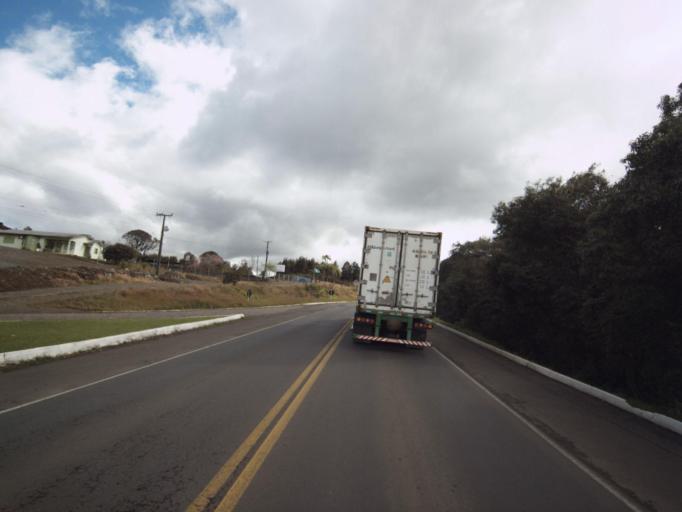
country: BR
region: Santa Catarina
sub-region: Concordia
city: Concordia
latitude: -27.2161
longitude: -51.9521
